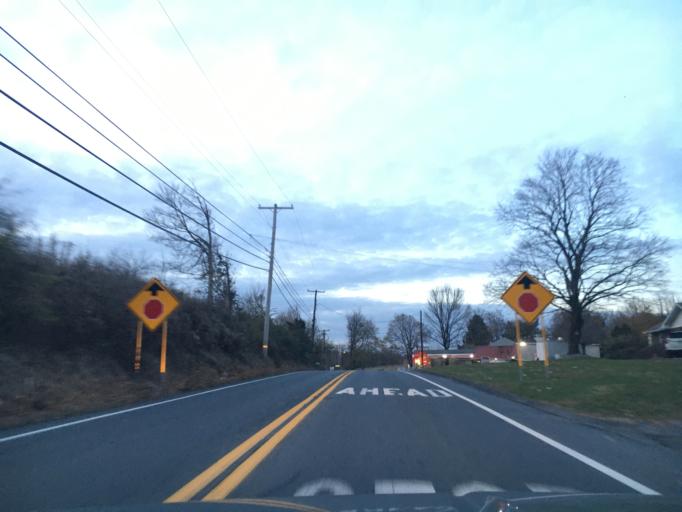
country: US
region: Pennsylvania
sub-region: Lehigh County
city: Schnecksville
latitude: 40.6773
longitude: -75.5702
